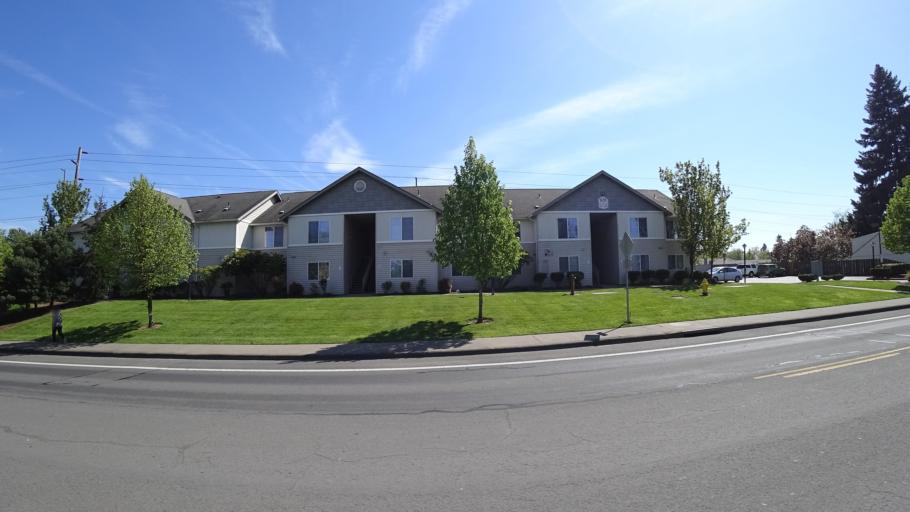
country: US
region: Oregon
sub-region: Washington County
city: Hillsboro
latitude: 45.5216
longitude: -122.9658
